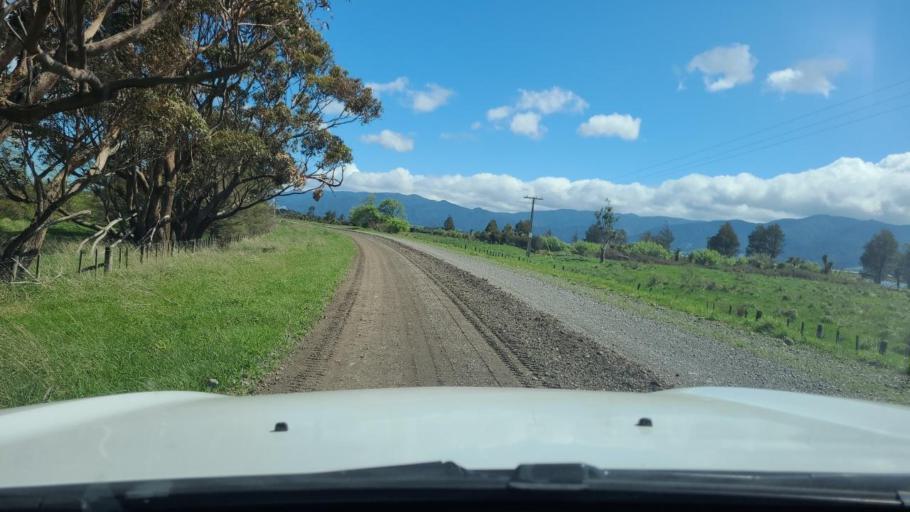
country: NZ
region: Wellington
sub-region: Upper Hutt City
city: Upper Hutt
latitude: -41.2421
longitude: 175.2666
